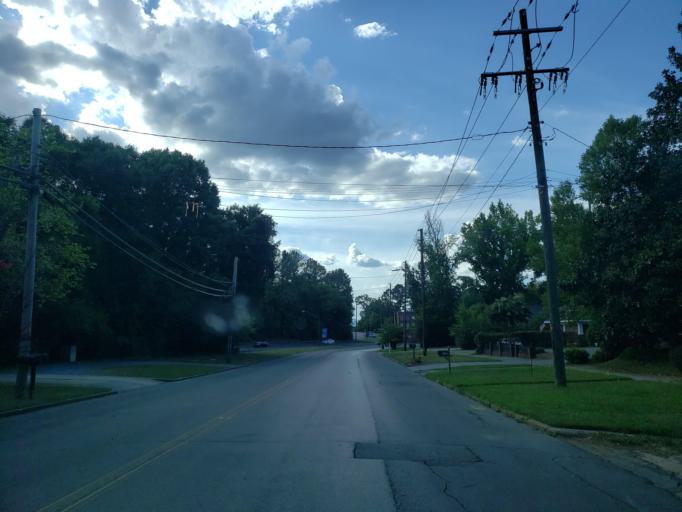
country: US
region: Georgia
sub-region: Floyd County
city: Rome
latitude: 34.2383
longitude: -85.1602
